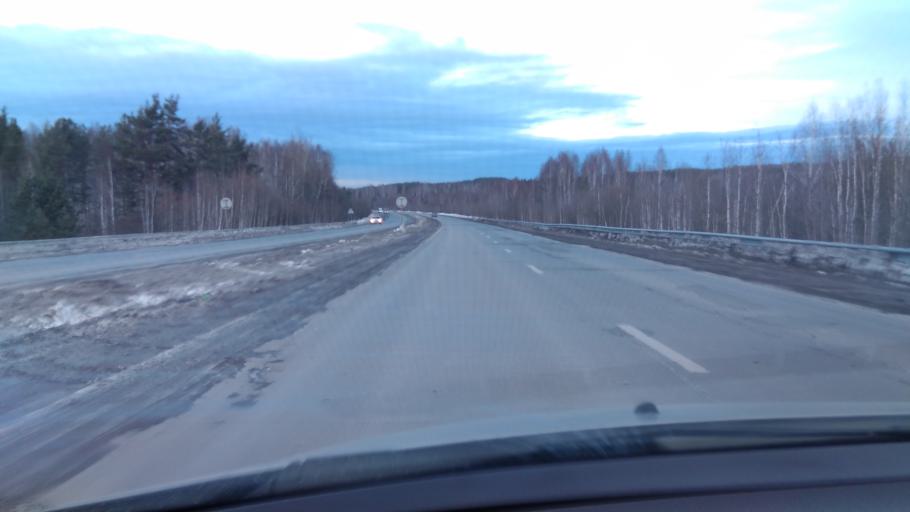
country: RU
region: Sverdlovsk
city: Shchelkun
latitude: 56.3192
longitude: 60.8698
